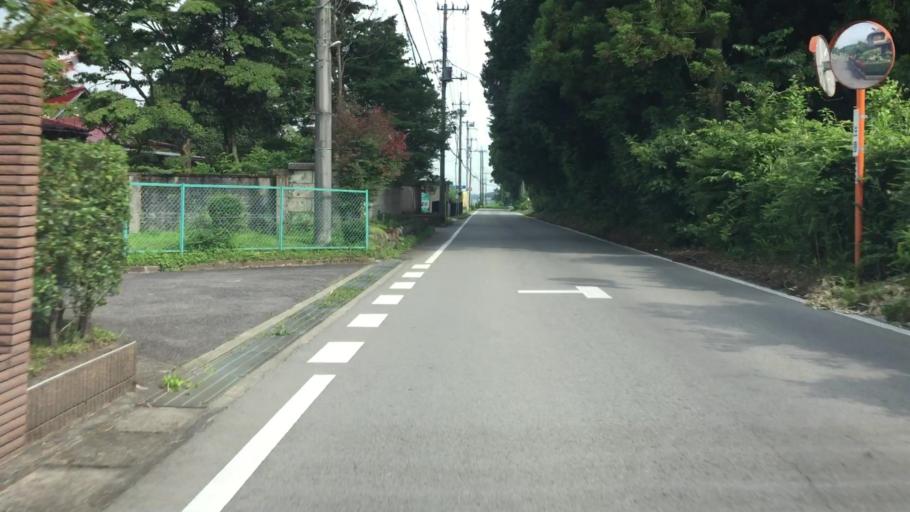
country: JP
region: Tochigi
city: Kuroiso
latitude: 36.9684
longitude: 139.9780
